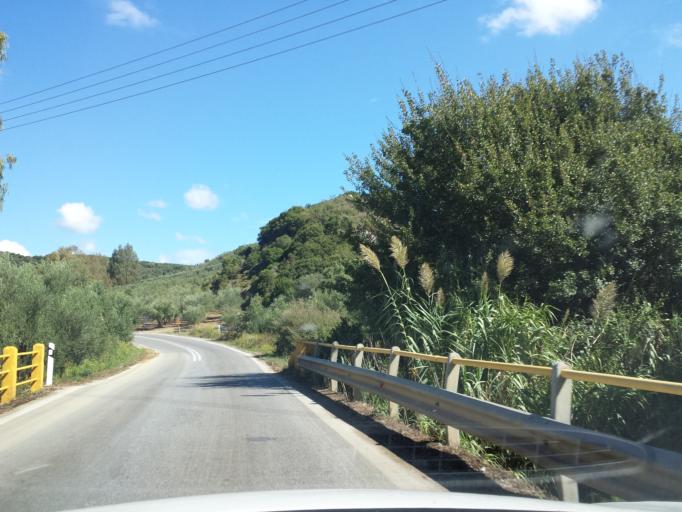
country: GR
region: Peloponnese
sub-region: Nomos Messinias
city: Pylos
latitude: 36.9375
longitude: 21.7412
